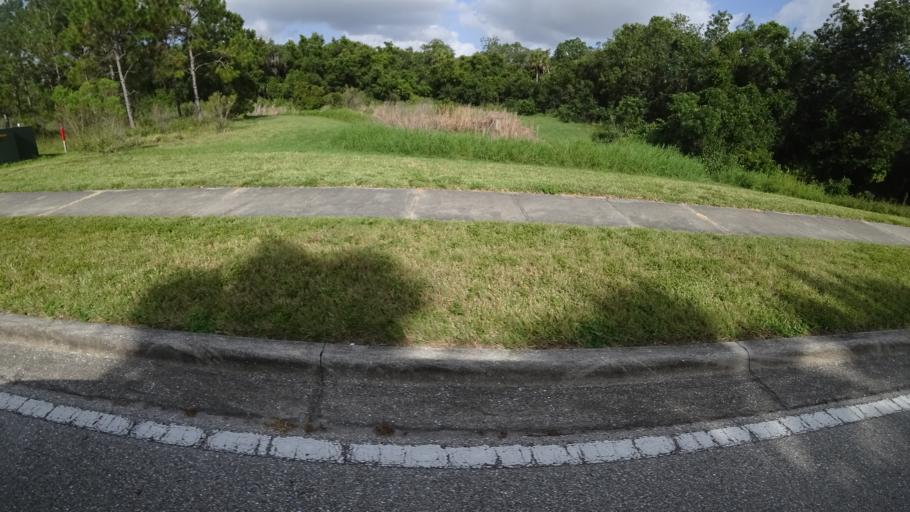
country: US
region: Florida
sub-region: Sarasota County
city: The Meadows
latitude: 27.4059
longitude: -82.4505
